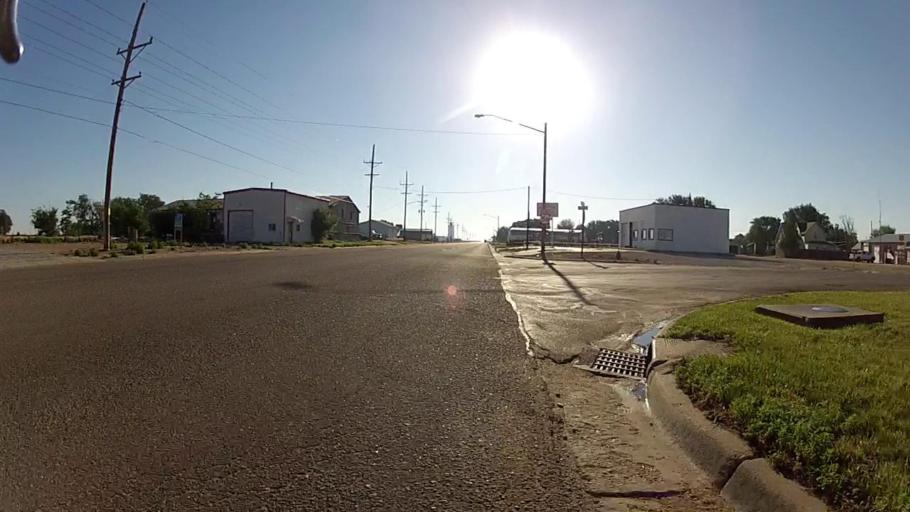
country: US
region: Kansas
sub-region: Haskell County
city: Sublette
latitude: 37.4834
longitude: -100.8427
